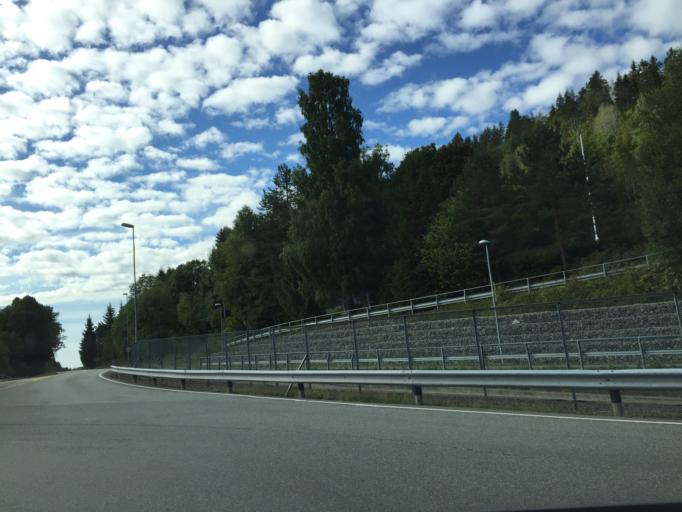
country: NO
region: Vestfold
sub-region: Holmestrand
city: Gullhaug
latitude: 59.5055
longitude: 10.1748
